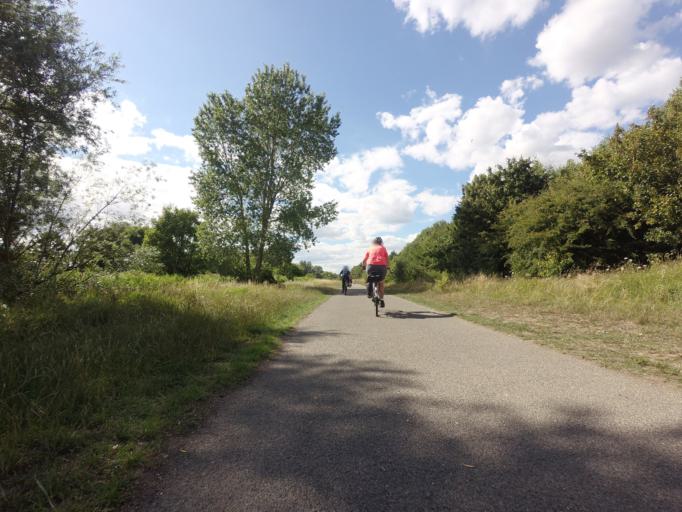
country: GB
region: England
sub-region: East Sussex
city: Eastbourne
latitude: 50.8037
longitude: 0.2870
